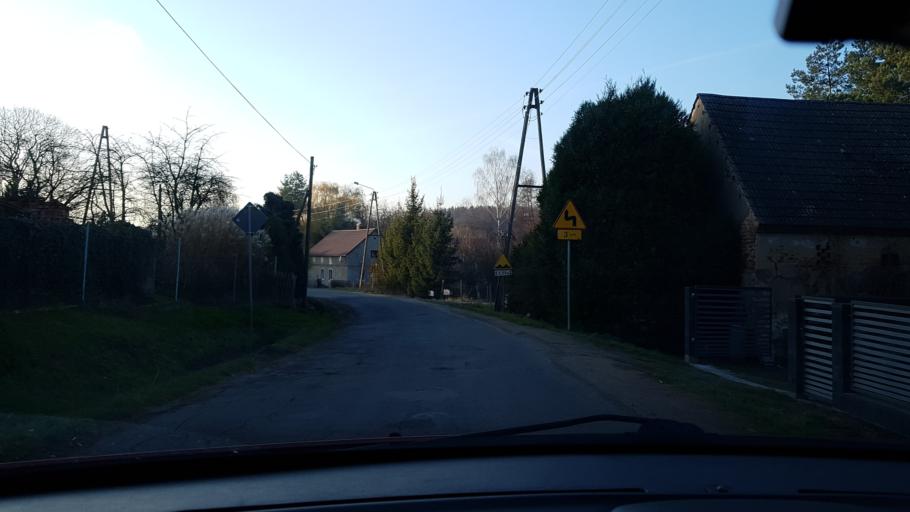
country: PL
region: Lower Silesian Voivodeship
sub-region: Powiat zabkowicki
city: Henrykow
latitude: 50.6584
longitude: 17.0777
